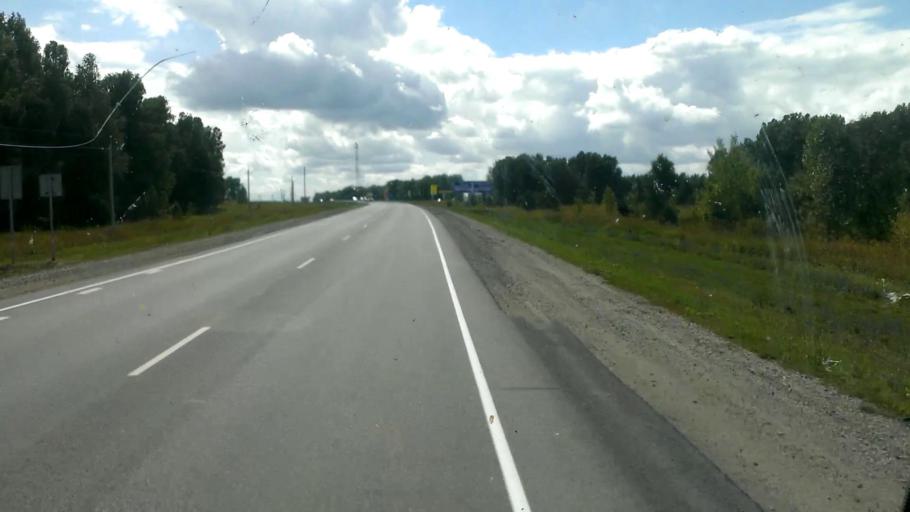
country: RU
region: Altai Krai
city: Troitskoye
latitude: 52.9722
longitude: 84.7479
